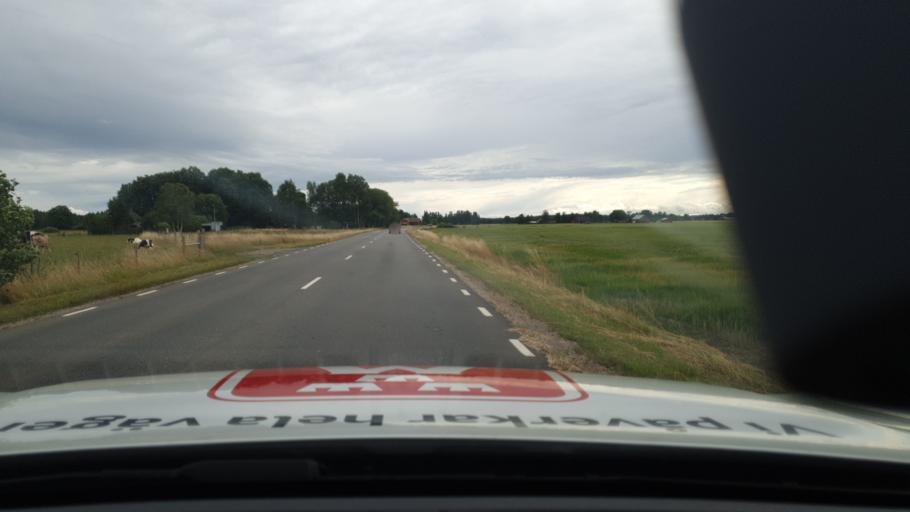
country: SE
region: Vaestra Goetaland
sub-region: Toreboda Kommun
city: Toereboda
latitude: 58.6718
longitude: 14.1333
